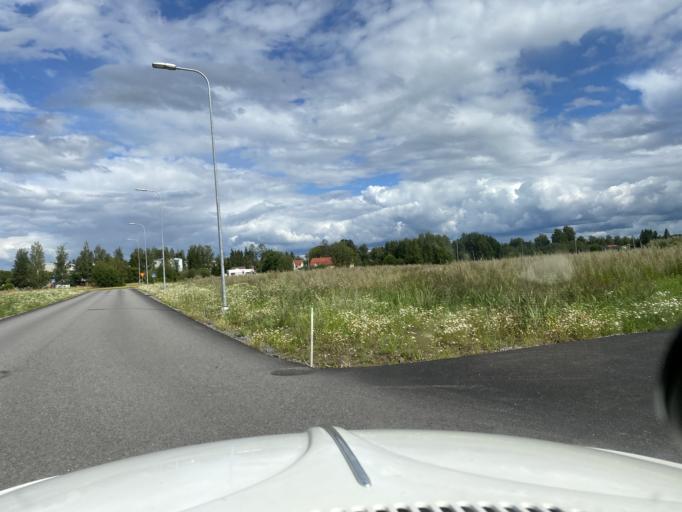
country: FI
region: Satakunta
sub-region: Pori
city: Huittinen
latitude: 61.1705
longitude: 22.6811
